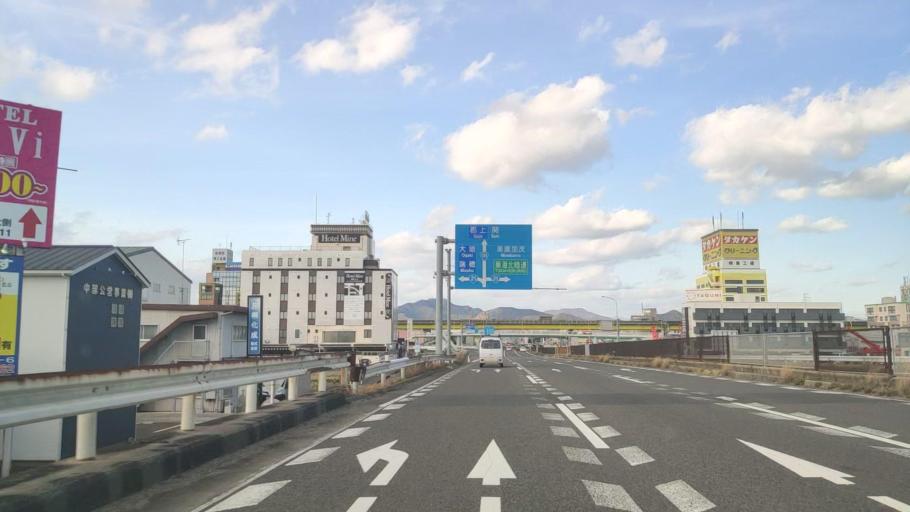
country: JP
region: Gifu
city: Kasamatsucho
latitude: 35.3854
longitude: 136.7845
